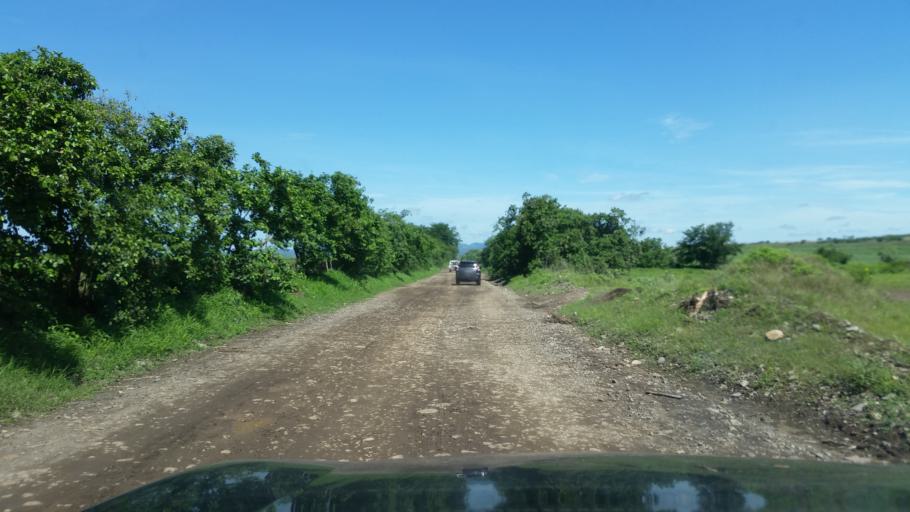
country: NI
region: Chinandega
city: Puerto Morazan
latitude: 12.7725
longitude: -87.0950
